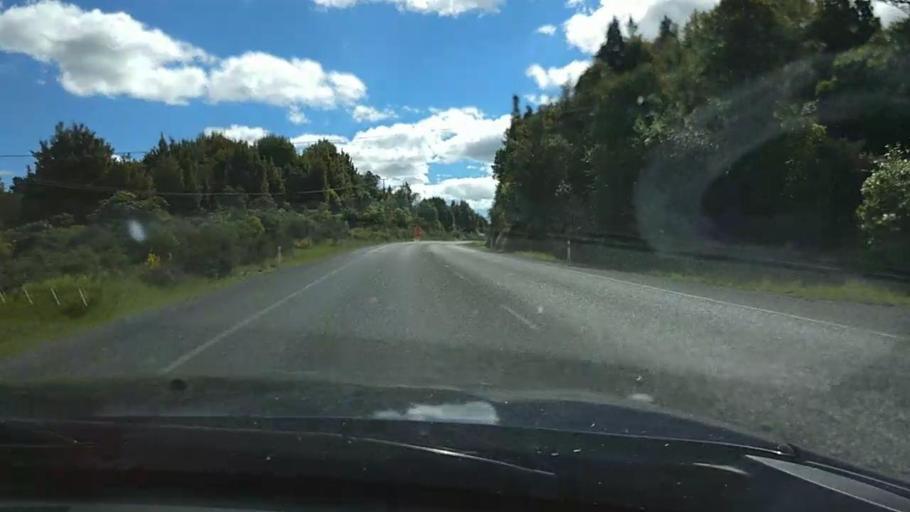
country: NZ
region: Bay of Plenty
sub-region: Rotorua District
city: Rotorua
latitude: -38.0716
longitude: 176.1307
